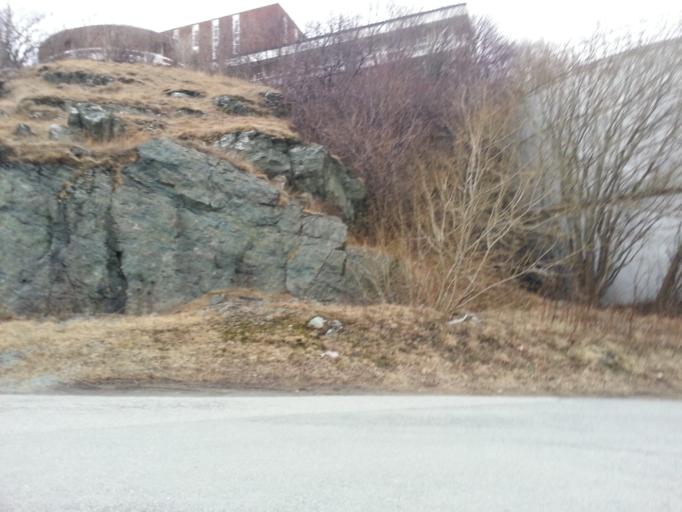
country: NO
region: Sor-Trondelag
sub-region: Trondheim
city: Trondheim
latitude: 63.4450
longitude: 10.4214
